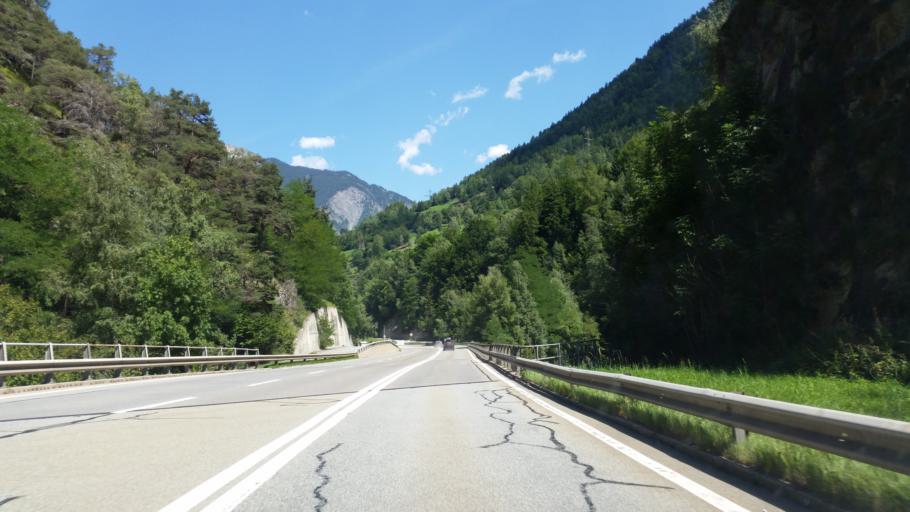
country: CH
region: Valais
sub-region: Entremont District
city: Orsieres
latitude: 46.0637
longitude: 7.1500
